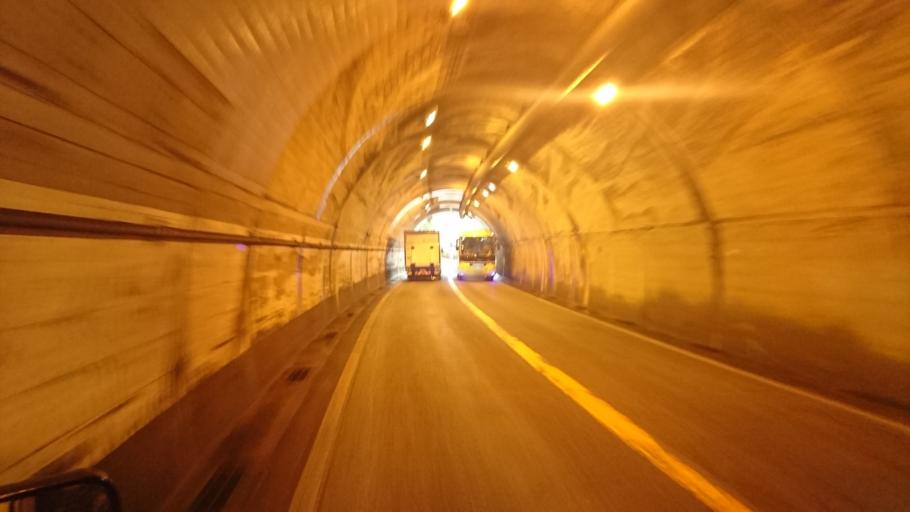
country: JP
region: Tottori
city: Tottori
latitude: 35.5450
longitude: 134.5031
